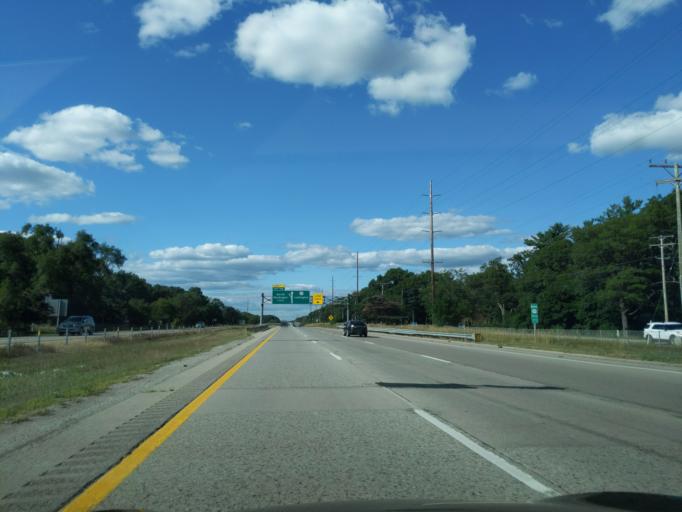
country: US
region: Michigan
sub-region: Muskegon County
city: Muskegon
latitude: 43.2390
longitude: -86.2045
